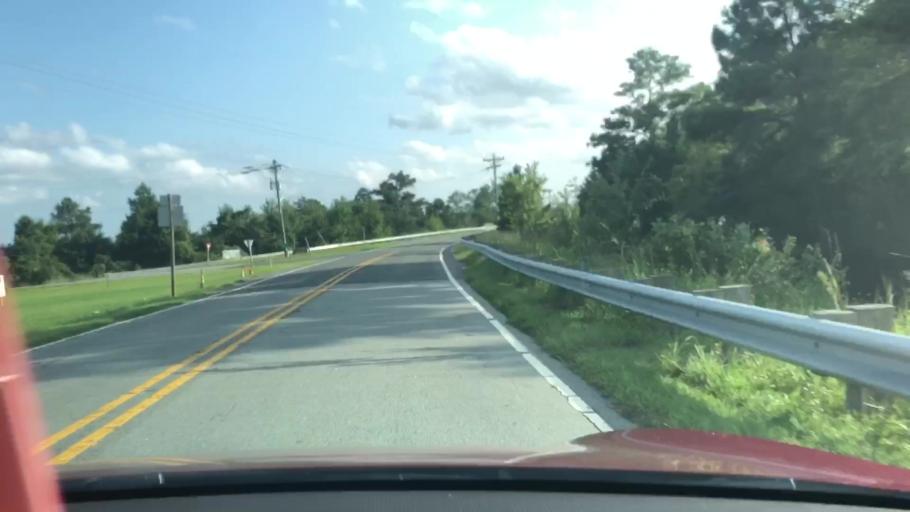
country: US
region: North Carolina
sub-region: Dare County
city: Wanchese
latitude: 35.7075
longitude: -75.7684
